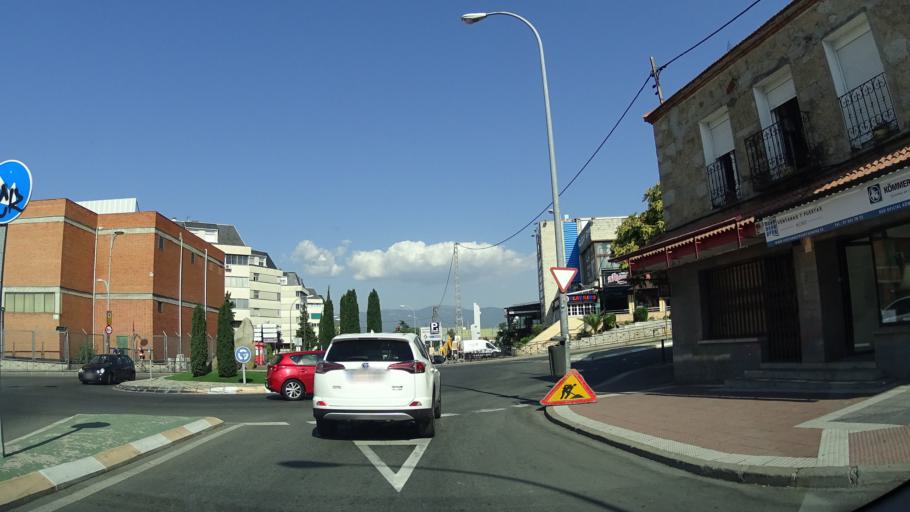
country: ES
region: Madrid
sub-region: Provincia de Madrid
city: Collado-Villalba
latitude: 40.6329
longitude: -4.0037
